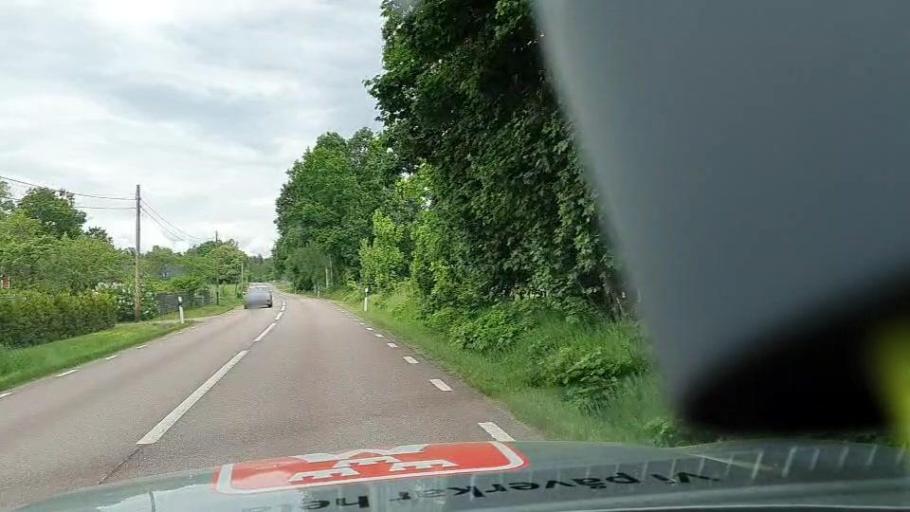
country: SE
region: Kalmar
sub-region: Emmaboda Kommun
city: Emmaboda
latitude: 56.4647
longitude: 15.5931
